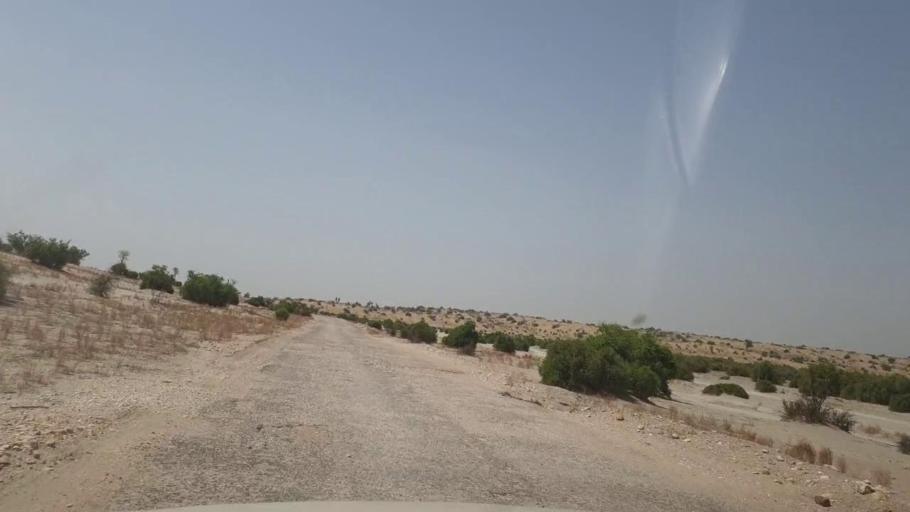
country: PK
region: Sindh
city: Khanpur
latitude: 27.3545
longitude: 69.3178
